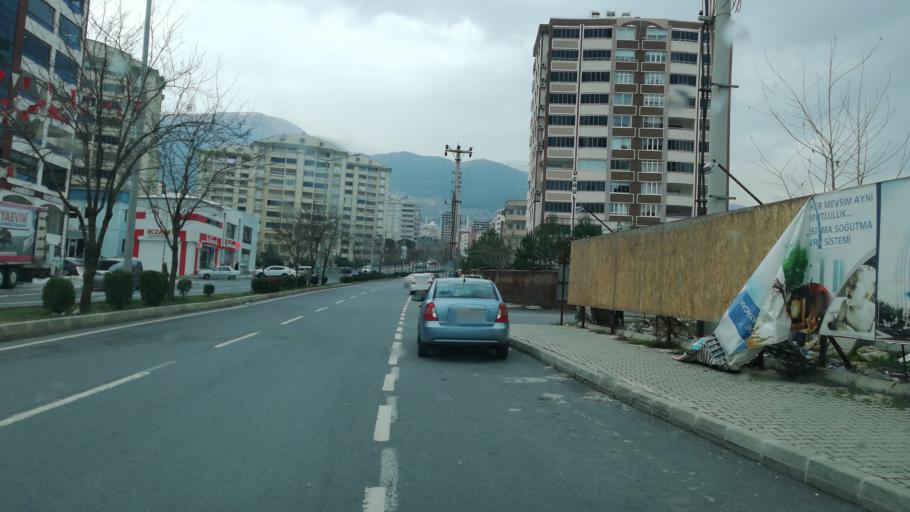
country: TR
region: Kahramanmaras
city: Kahramanmaras
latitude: 37.5859
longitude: 36.8613
